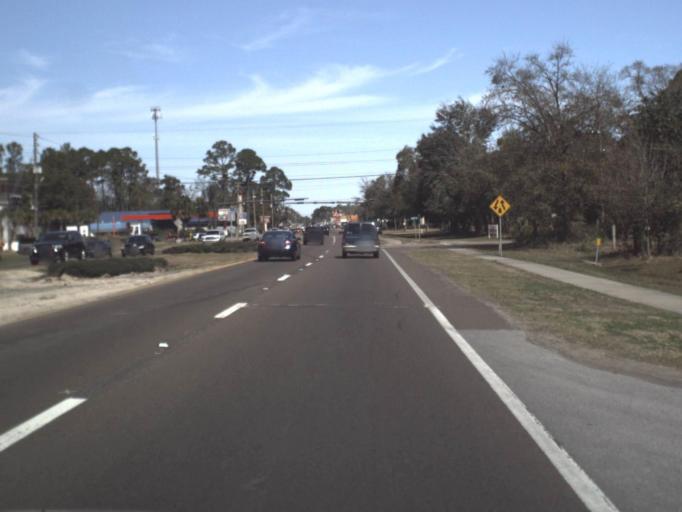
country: US
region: Florida
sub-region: Bay County
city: Lynn Haven
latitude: 30.2313
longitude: -85.6489
